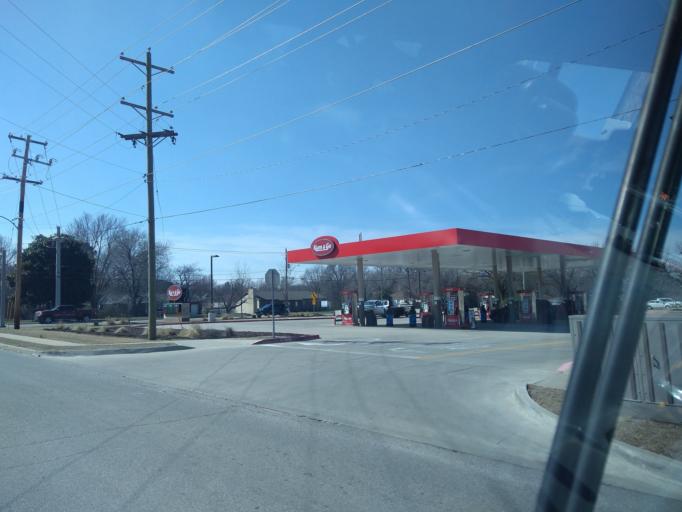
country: US
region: Arkansas
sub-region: Washington County
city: Farmington
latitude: 36.0433
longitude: -94.2361
